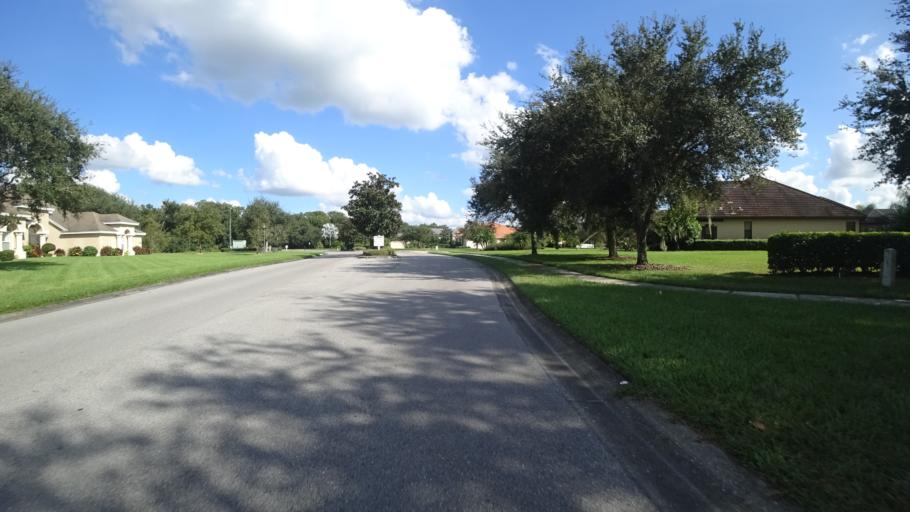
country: US
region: Florida
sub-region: Manatee County
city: Ellenton
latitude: 27.5480
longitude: -82.3886
